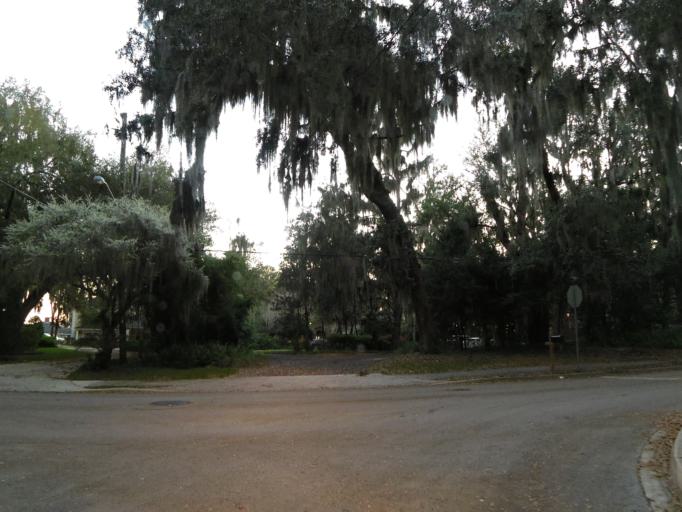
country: US
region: Florida
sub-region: Clay County
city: Orange Park
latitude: 30.1544
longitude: -81.7022
